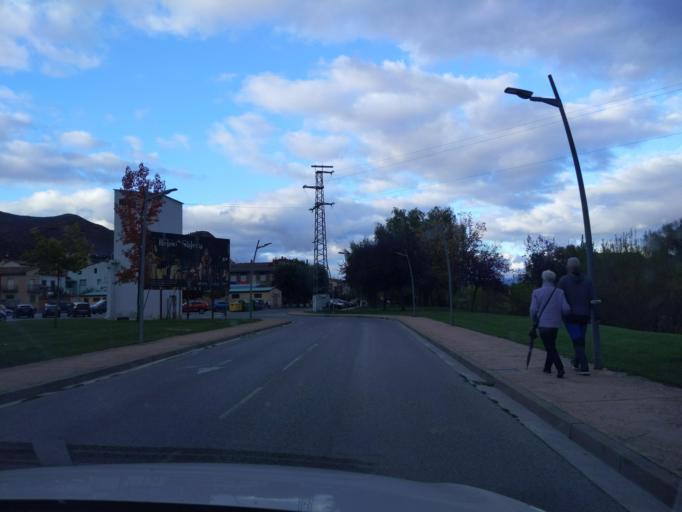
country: ES
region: La Rioja
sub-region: Provincia de La Rioja
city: Najera
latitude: 42.4141
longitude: -2.7339
